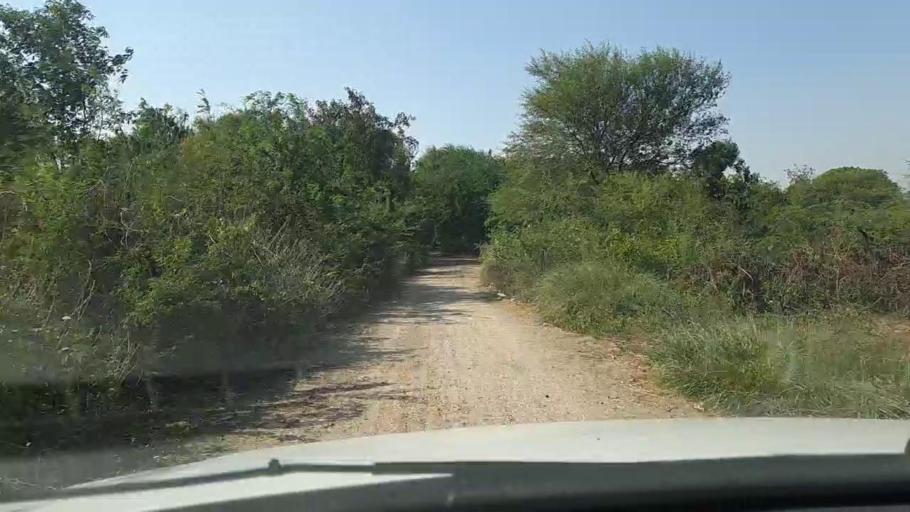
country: PK
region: Sindh
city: Daro Mehar
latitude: 24.6951
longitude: 68.1652
